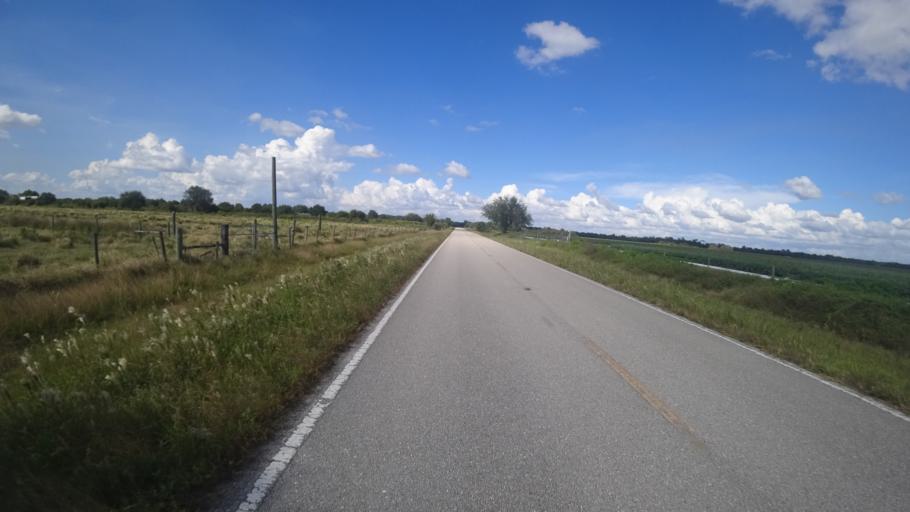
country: US
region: Florida
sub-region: DeSoto County
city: Arcadia
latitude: 27.2835
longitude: -82.0563
